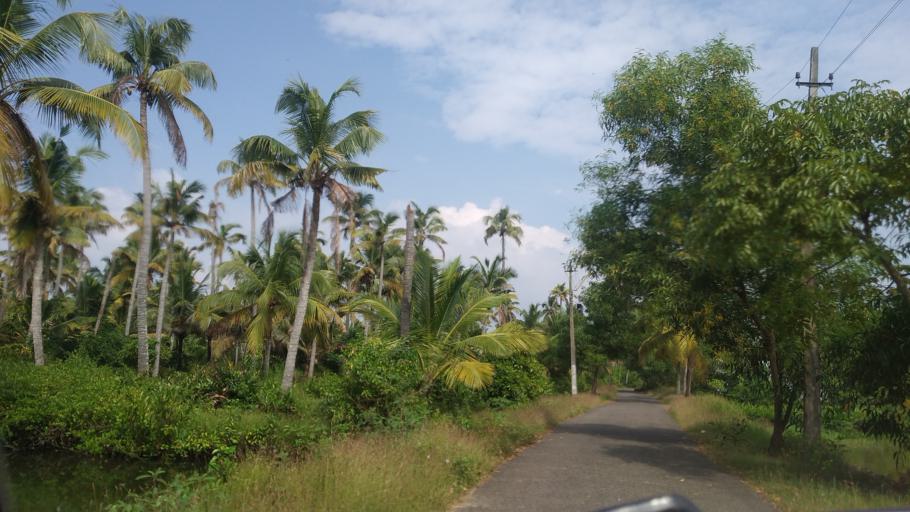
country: IN
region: Kerala
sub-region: Ernakulam
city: Elur
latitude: 10.0867
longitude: 76.1950
